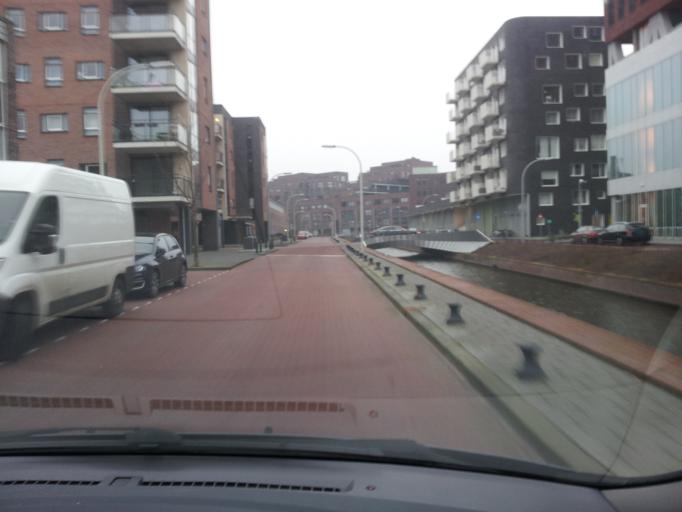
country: NL
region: South Holland
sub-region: Gemeente Den Haag
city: Ypenburg
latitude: 52.0537
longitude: 4.3917
